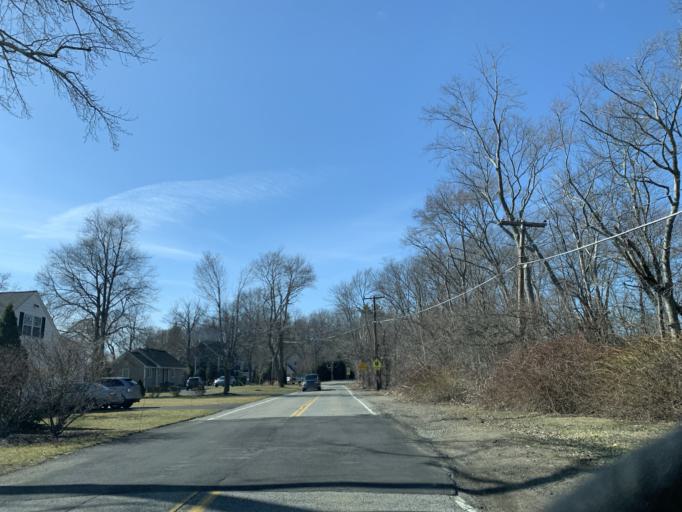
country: US
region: Massachusetts
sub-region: Norfolk County
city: Norwood
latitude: 42.1826
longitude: -71.2187
